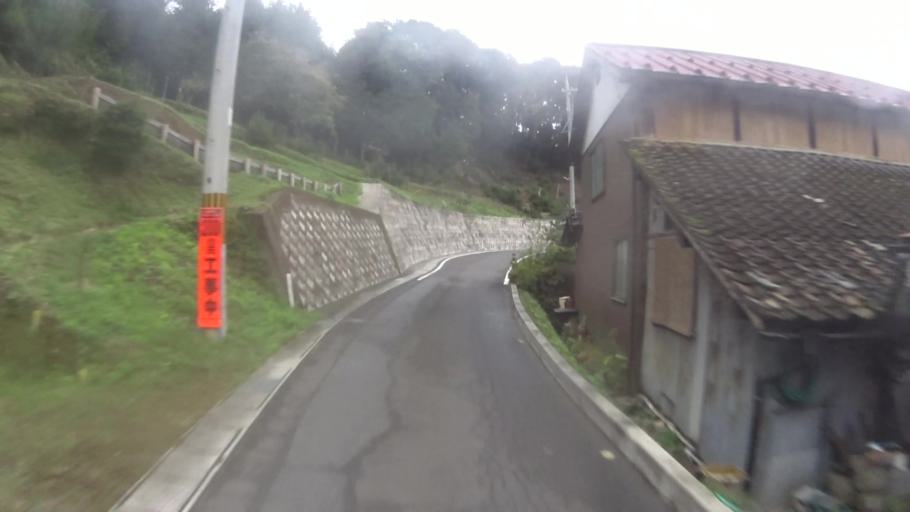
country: JP
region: Kyoto
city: Miyazu
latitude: 35.5295
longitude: 135.2287
